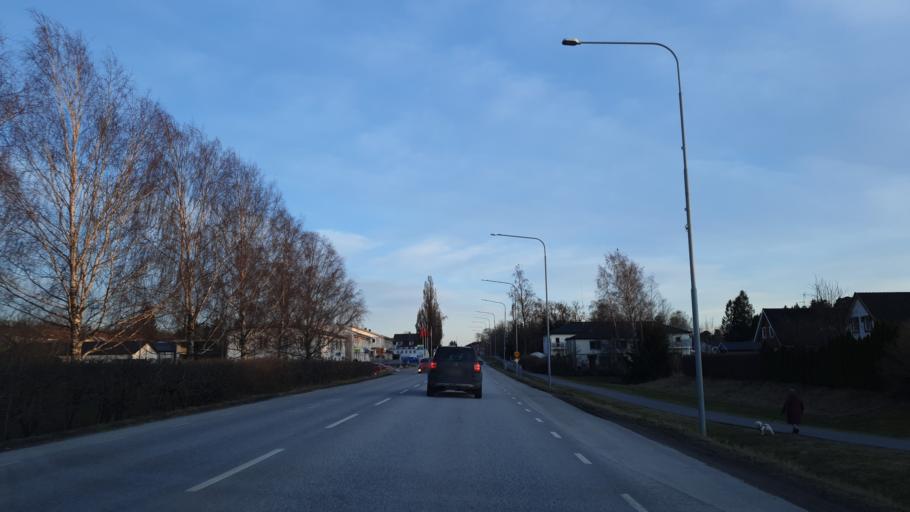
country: SE
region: Uppsala
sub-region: Habo Kommun
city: Balsta
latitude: 59.5822
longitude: 17.5084
